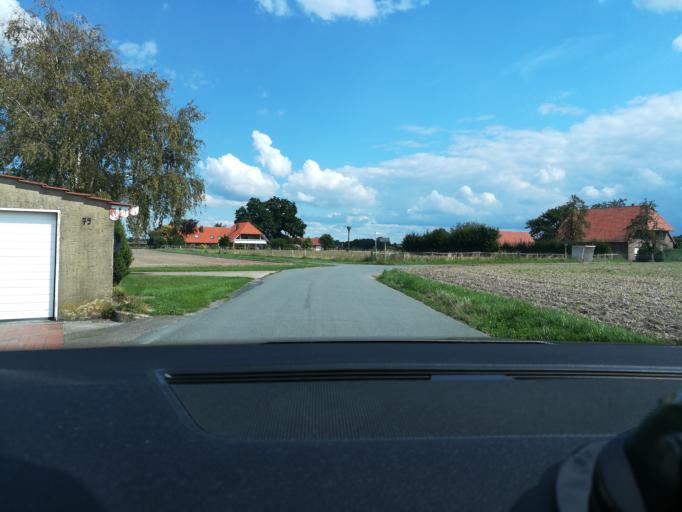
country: DE
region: North Rhine-Westphalia
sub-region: Regierungsbezirk Detmold
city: Hille
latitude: 52.3357
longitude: 8.6970
